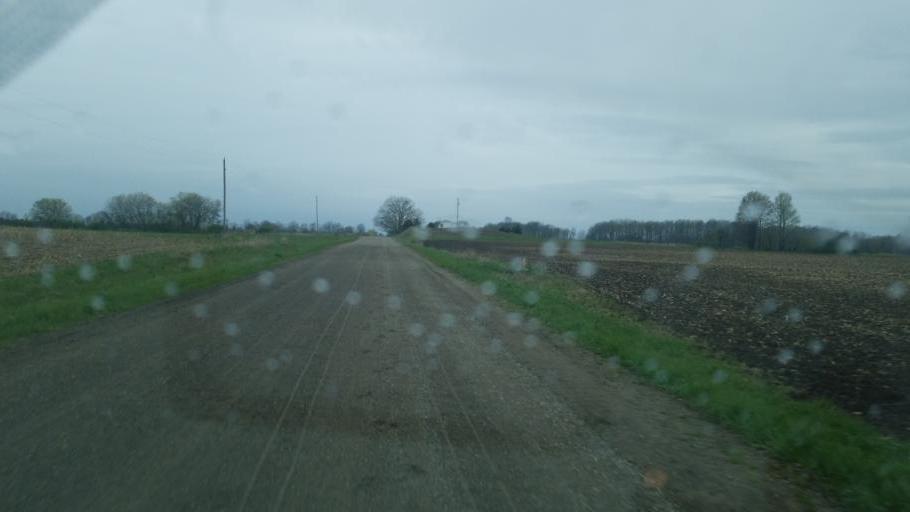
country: US
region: Michigan
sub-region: Montcalm County
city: Lakeview
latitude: 43.5110
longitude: -85.2719
